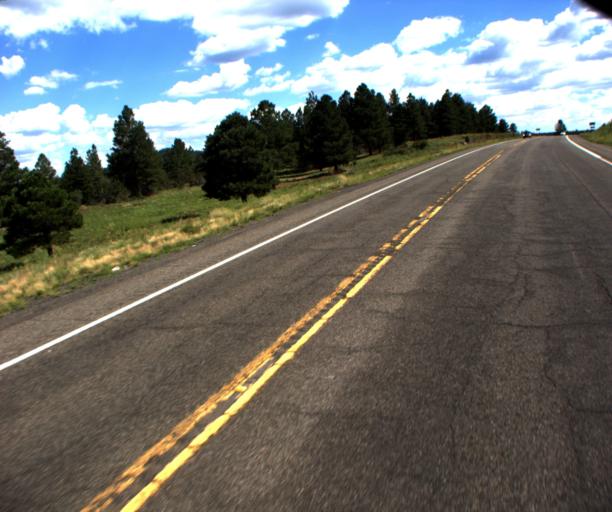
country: US
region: Arizona
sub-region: Coconino County
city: Williams
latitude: 35.2978
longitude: -112.1416
